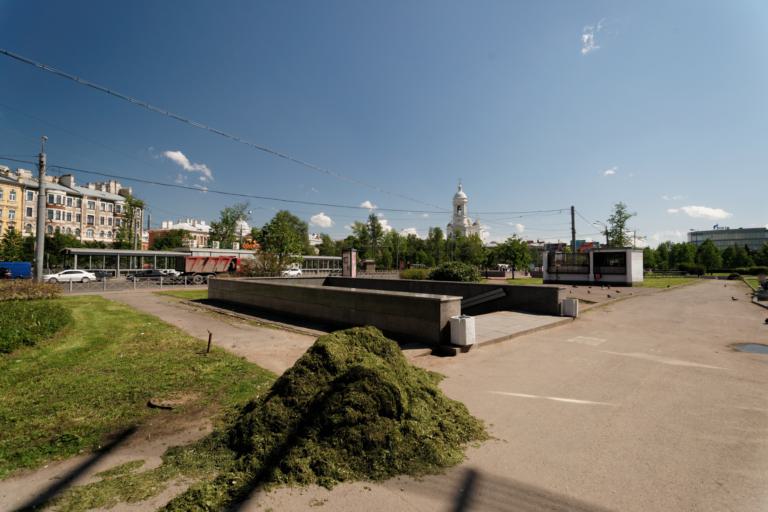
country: RU
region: St.-Petersburg
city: Petrogradka
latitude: 59.9518
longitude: 30.2905
